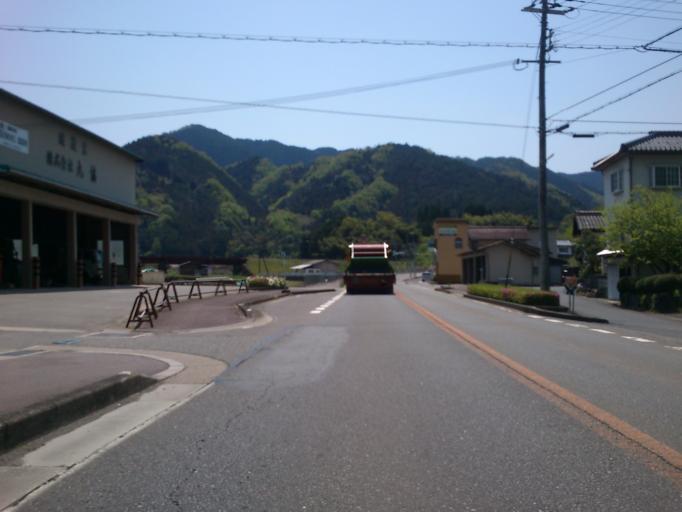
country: JP
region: Kyoto
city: Fukuchiyama
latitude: 35.3253
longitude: 135.0480
